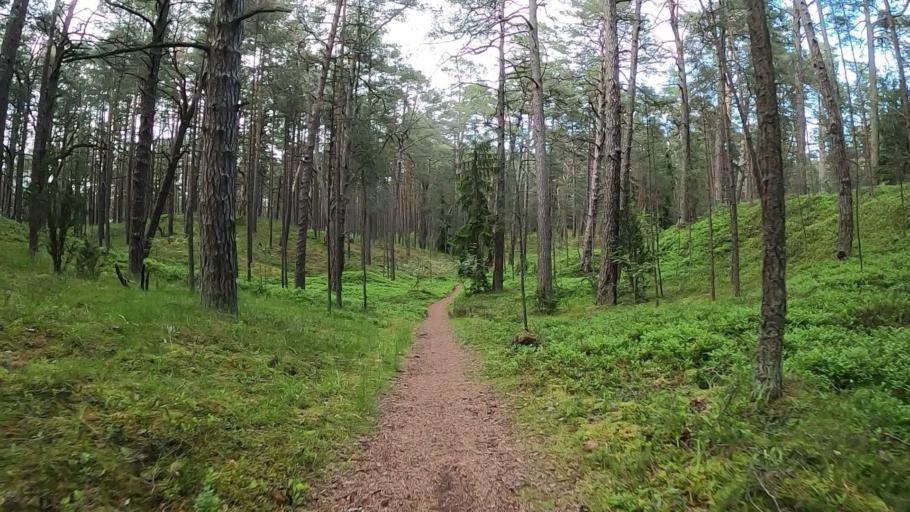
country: LV
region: Carnikava
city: Carnikava
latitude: 57.1212
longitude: 24.2093
